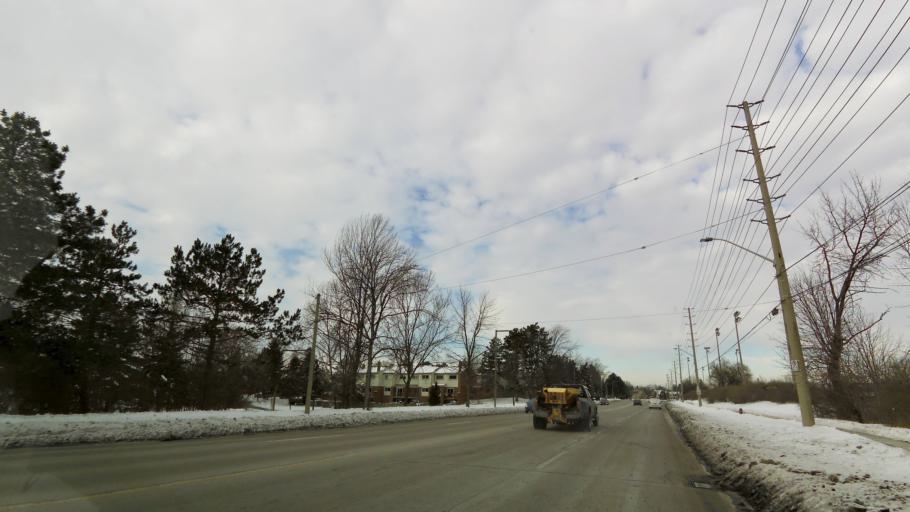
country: CA
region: Ontario
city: Mississauga
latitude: 43.5390
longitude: -79.6887
